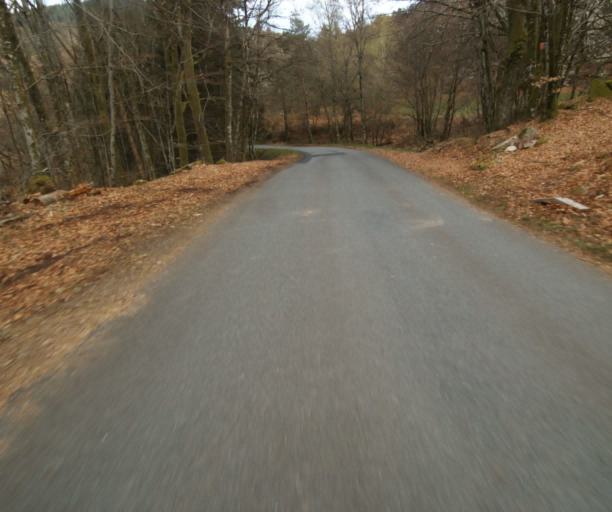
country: FR
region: Limousin
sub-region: Departement de la Correze
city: Correze
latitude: 45.4177
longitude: 1.8985
